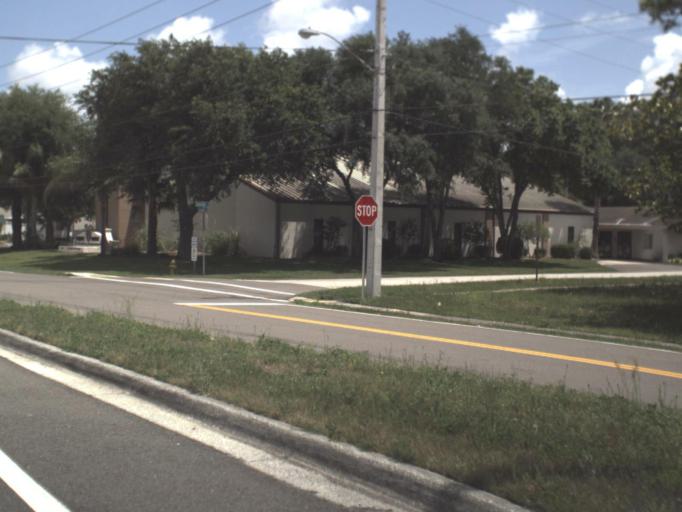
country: US
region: Florida
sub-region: Duval County
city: Jacksonville
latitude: 30.3144
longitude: -81.5587
